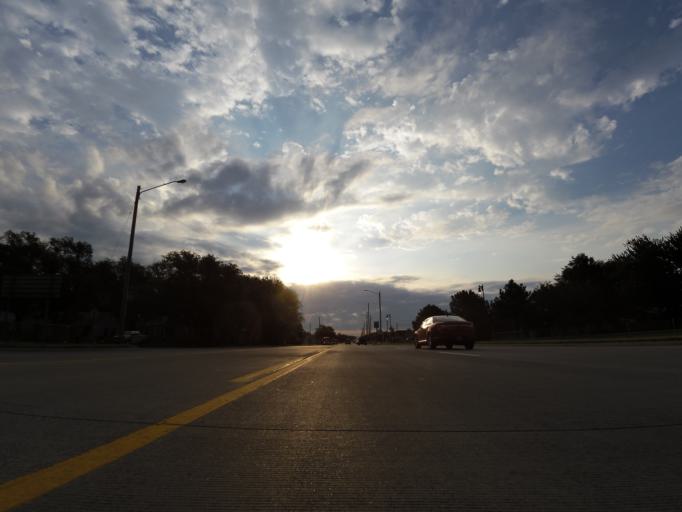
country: US
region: Kansas
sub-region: Sedgwick County
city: Wichita
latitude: 37.7226
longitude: -97.3161
